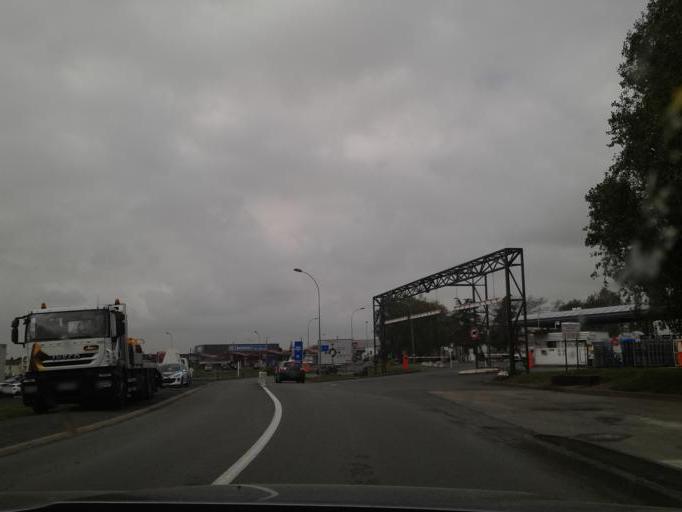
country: FR
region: Pays de la Loire
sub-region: Departement de la Vendee
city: Fontenay-le-Comte
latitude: 46.4513
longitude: -0.8055
